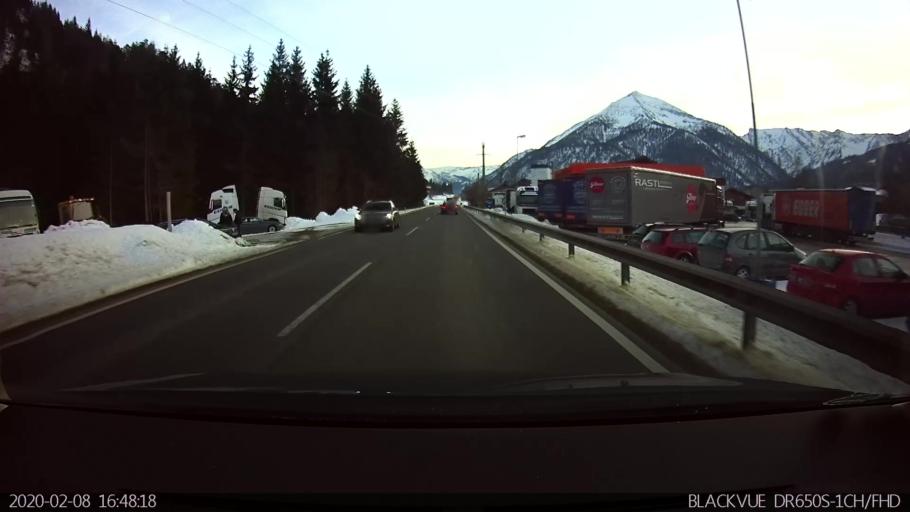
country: AT
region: Tyrol
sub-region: Politischer Bezirk Schwaz
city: Achenkirch
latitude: 47.5164
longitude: 11.7088
